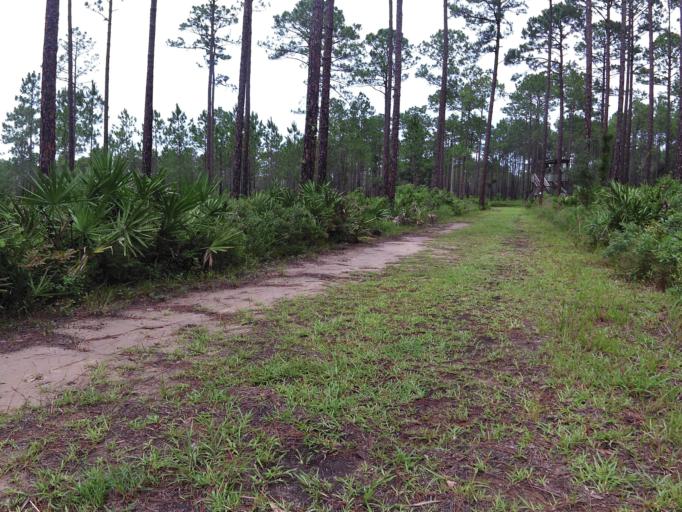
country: US
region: Florida
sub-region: Clay County
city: Green Cove Springs
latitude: 29.9674
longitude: -81.6295
